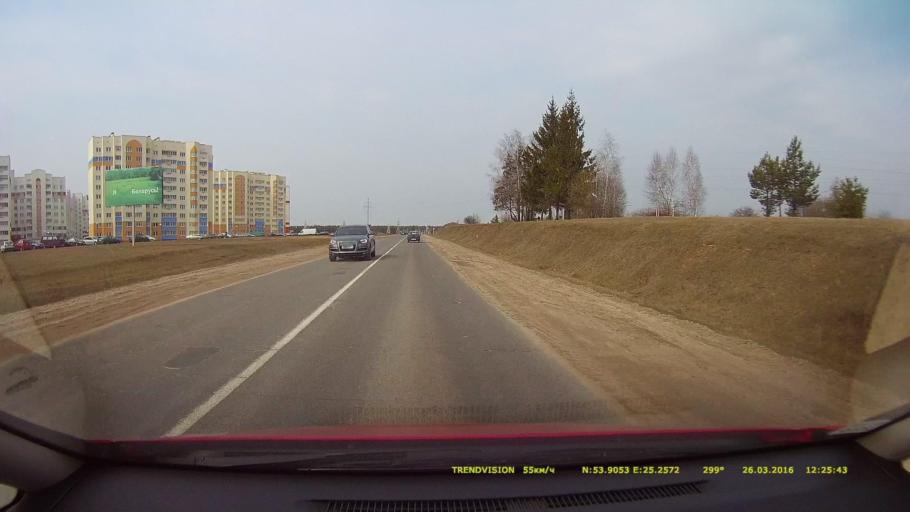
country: BY
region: Grodnenskaya
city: Lida
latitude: 53.9054
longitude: 25.2571
